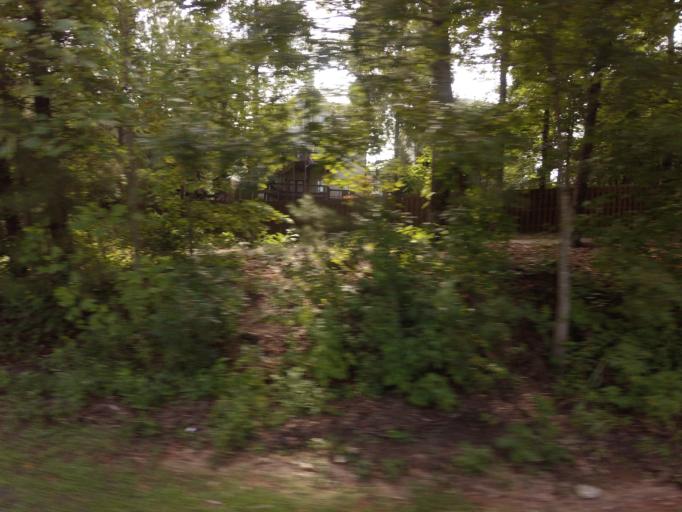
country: US
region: Georgia
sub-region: Fulton County
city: Johns Creek
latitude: 34.0382
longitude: -84.2347
